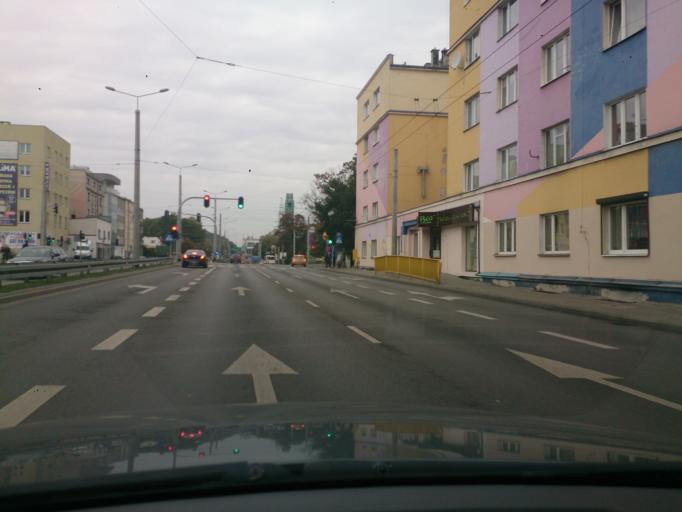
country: PL
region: Pomeranian Voivodeship
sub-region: Gdynia
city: Gdynia
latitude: 54.5308
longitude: 18.4976
